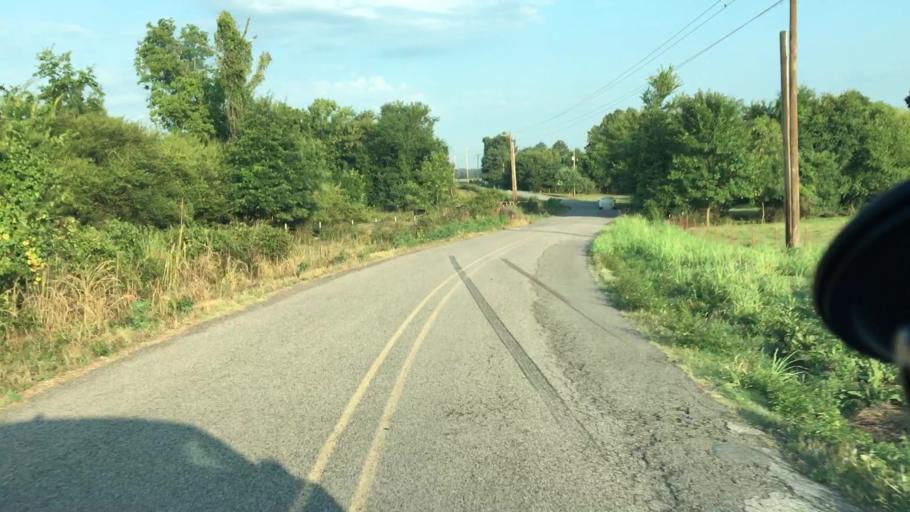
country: US
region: Arkansas
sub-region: Johnson County
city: Coal Hill
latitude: 35.3660
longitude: -93.5944
